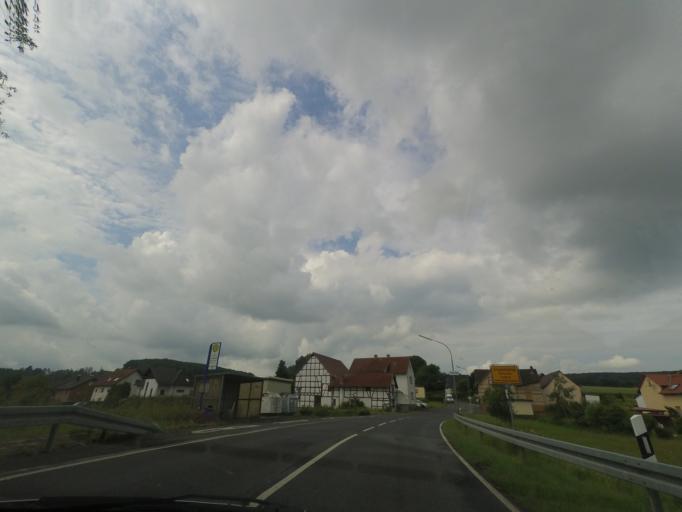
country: DE
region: Hesse
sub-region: Regierungsbezirk Giessen
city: Lohra
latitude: 50.7195
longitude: 8.6480
